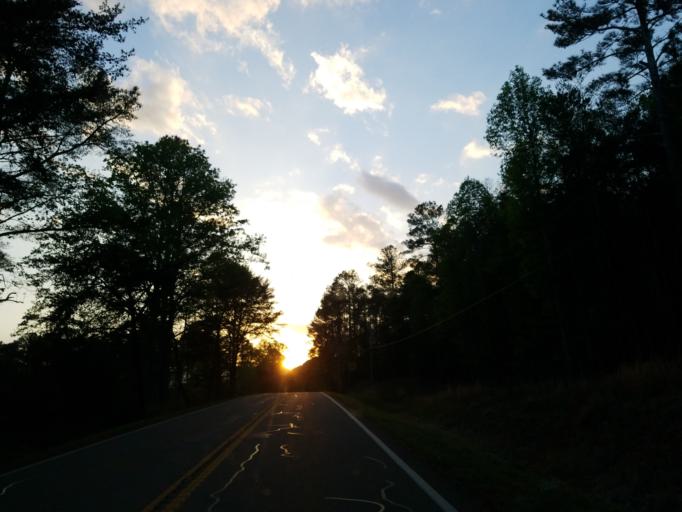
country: US
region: Georgia
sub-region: Pickens County
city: Jasper
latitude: 34.5121
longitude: -84.4458
